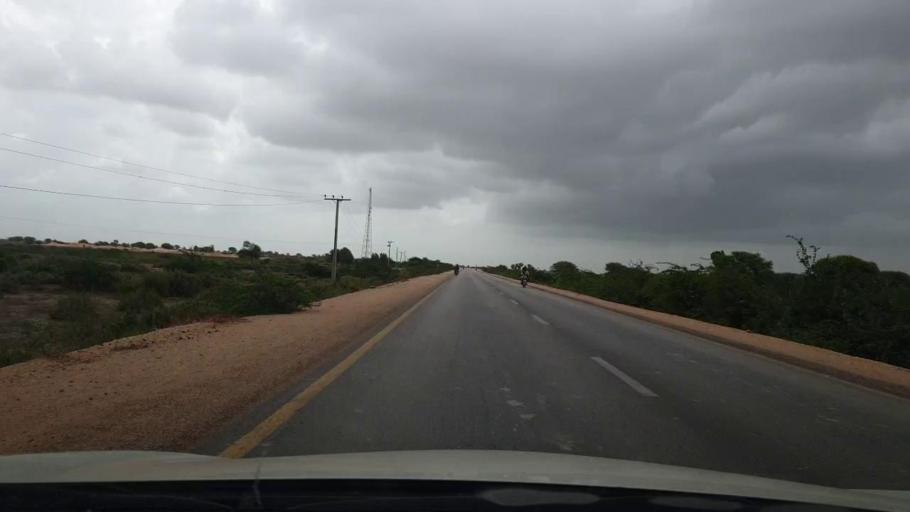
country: PK
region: Sindh
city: Mirpur Batoro
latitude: 24.6439
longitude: 68.4271
